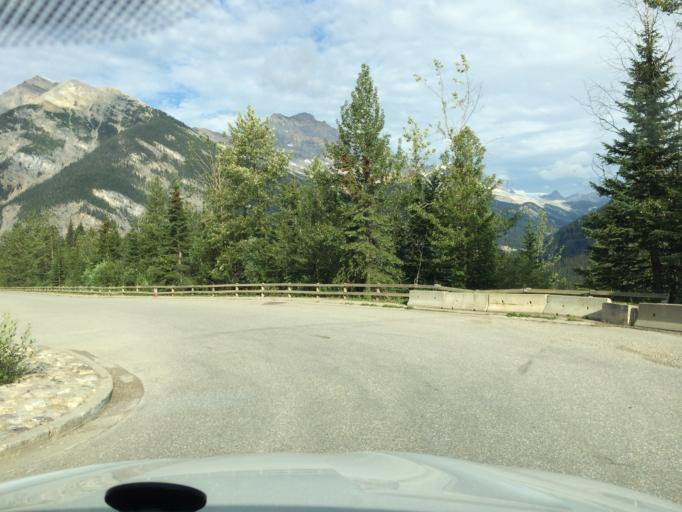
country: CA
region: Alberta
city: Lake Louise
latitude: 51.4316
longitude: -116.3994
